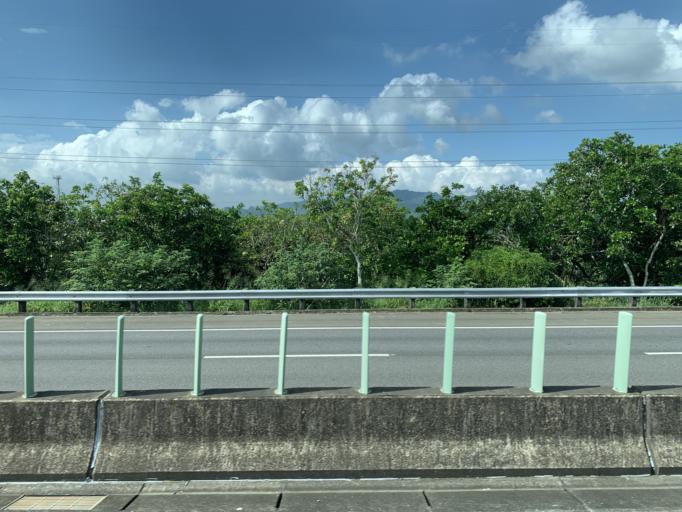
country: TW
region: Taiwan
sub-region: Pingtung
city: Pingtung
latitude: 22.8565
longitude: 120.4945
